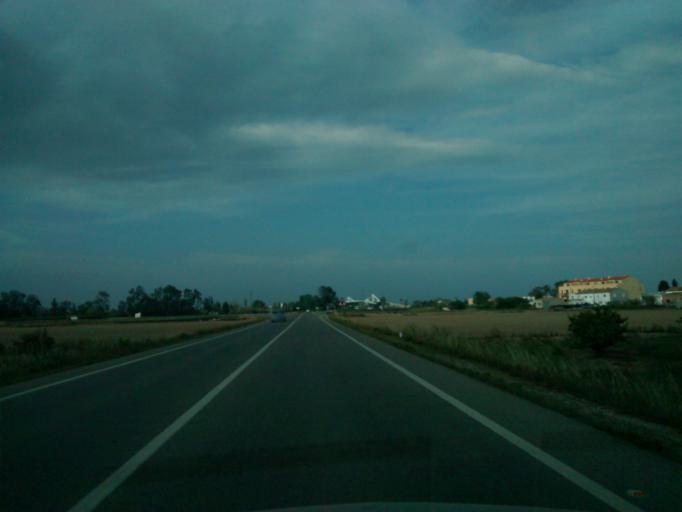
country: ES
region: Catalonia
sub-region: Provincia de Tarragona
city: Deltebre
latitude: 40.7071
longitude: 0.7124
